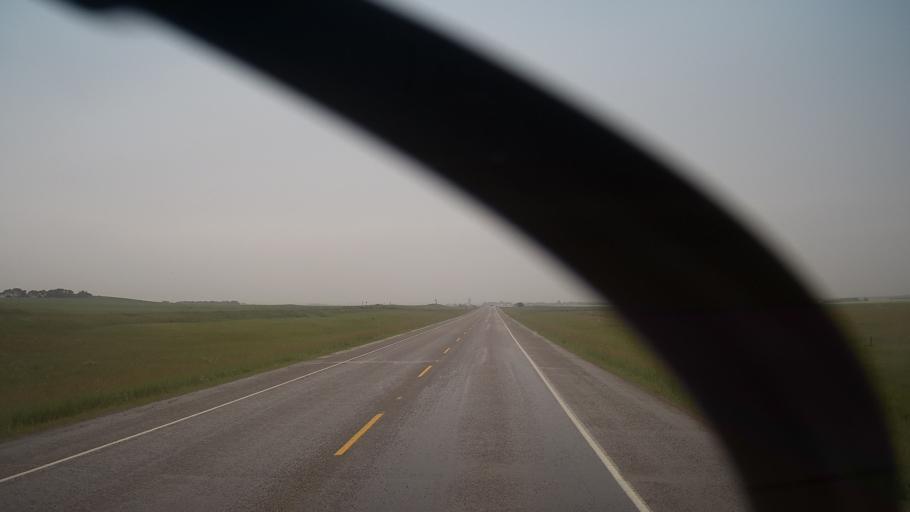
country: CA
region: Saskatchewan
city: Wilkie
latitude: 52.1866
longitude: -108.4030
